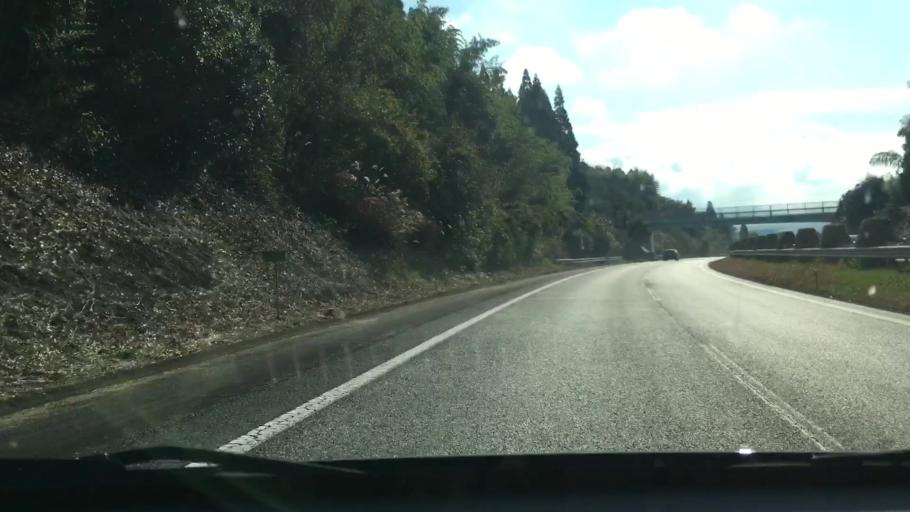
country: JP
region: Kumamoto
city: Matsubase
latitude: 32.6089
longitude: 130.7243
